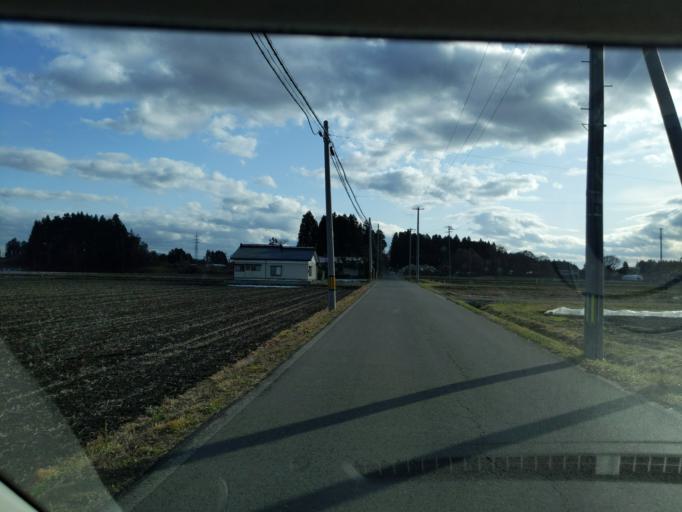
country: JP
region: Iwate
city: Mizusawa
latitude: 39.1304
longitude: 141.0808
